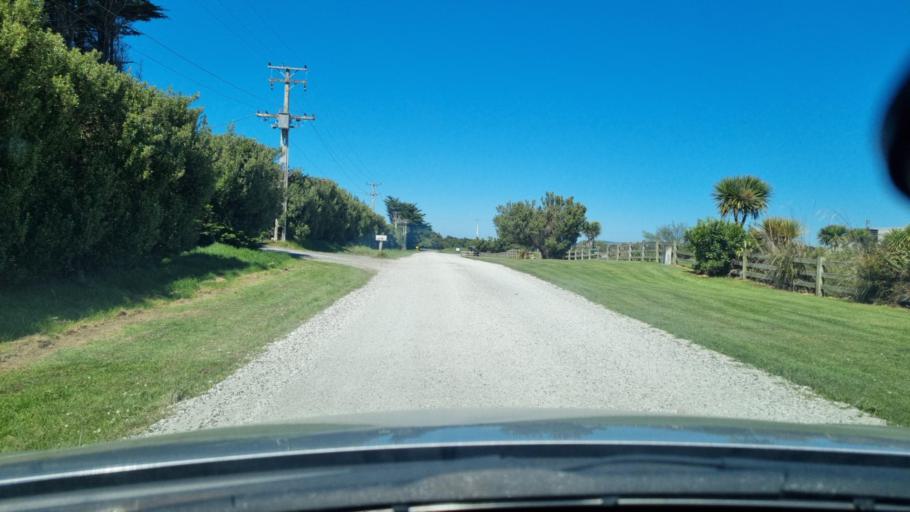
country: NZ
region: Southland
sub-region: Invercargill City
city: Invercargill
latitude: -46.4429
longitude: 168.2784
